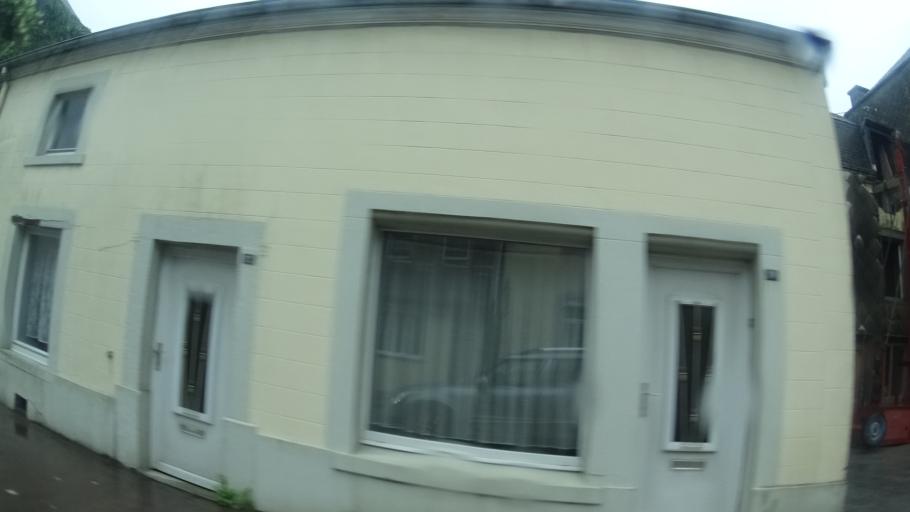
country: BE
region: Wallonia
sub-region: Province du Luxembourg
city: Bertrix
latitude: 49.8553
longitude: 5.2511
